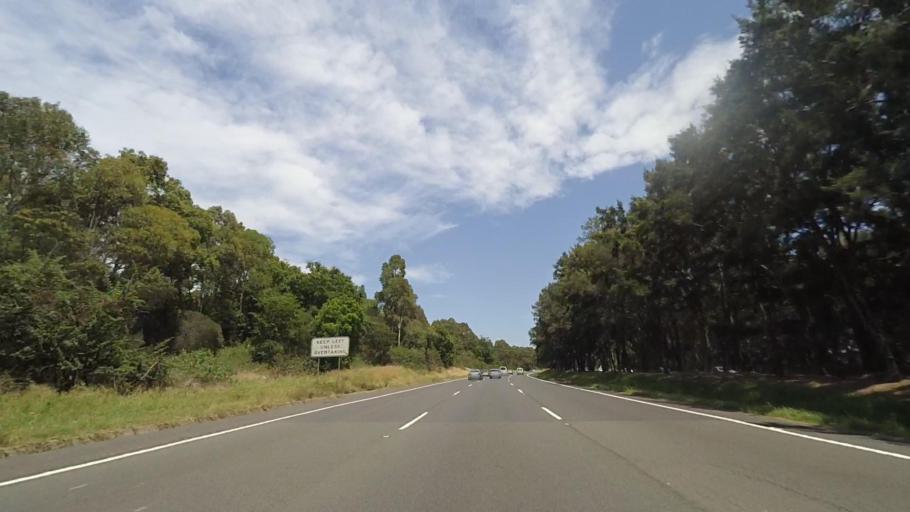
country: AU
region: New South Wales
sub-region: Wollongong
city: Berkeley
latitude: -34.4634
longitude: 150.8503
